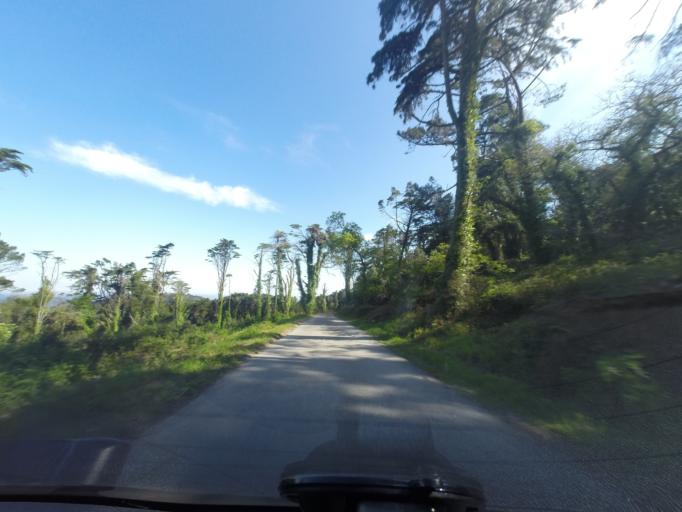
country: PT
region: Lisbon
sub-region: Sintra
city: Colares
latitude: 38.7710
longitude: -9.4583
